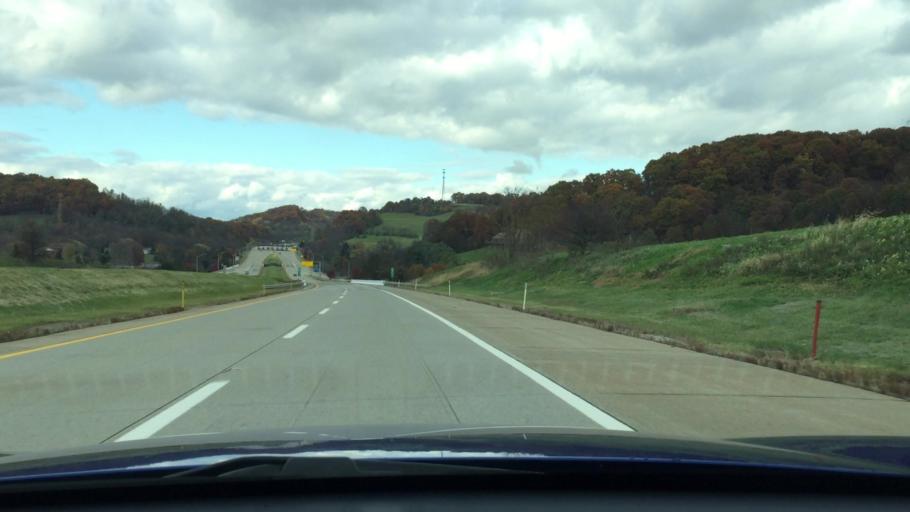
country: US
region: Pennsylvania
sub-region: Westmoreland County
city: Jeannette
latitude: 40.2777
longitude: -79.6124
